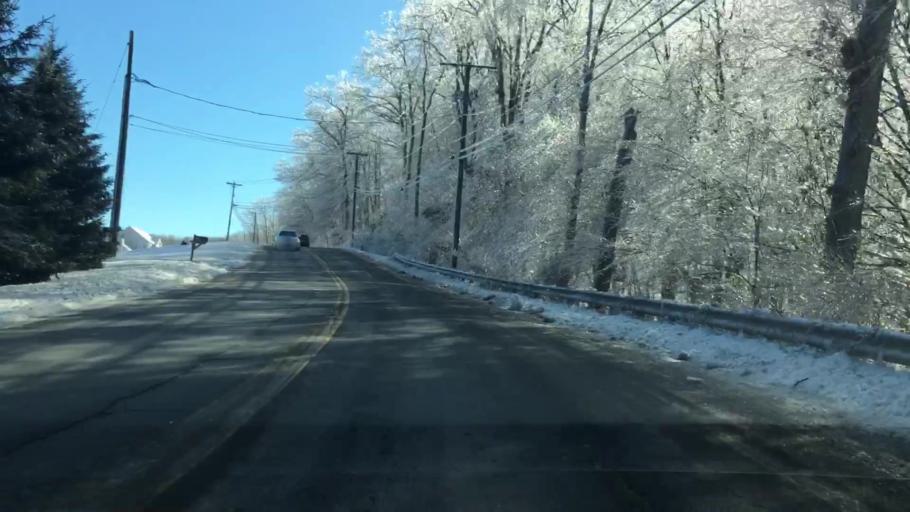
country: US
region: Connecticut
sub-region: Fairfield County
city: Newtown
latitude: 41.4039
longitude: -73.2634
